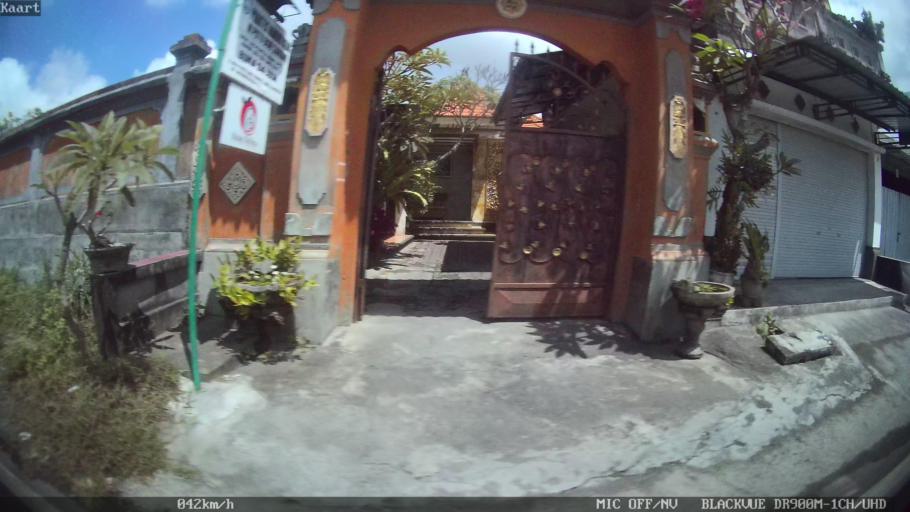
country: ID
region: Bali
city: Banjar Pasekan
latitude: -8.5846
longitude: 115.2953
